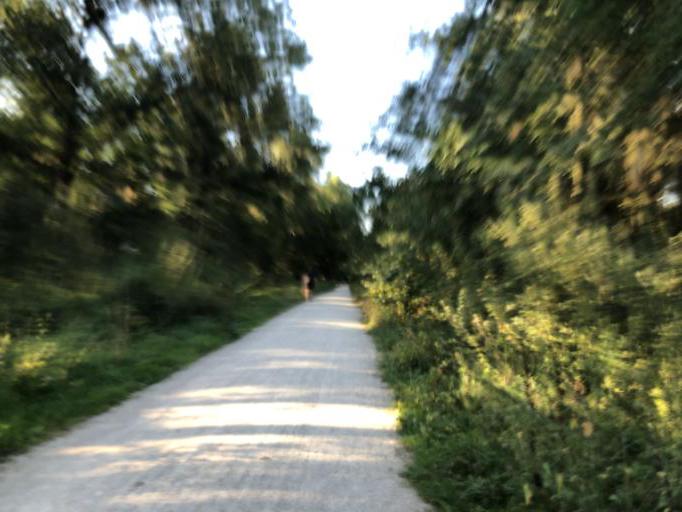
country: DE
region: Bavaria
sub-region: Regierungsbezirk Mittelfranken
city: Buckenhof
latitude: 49.5866
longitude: 11.0482
